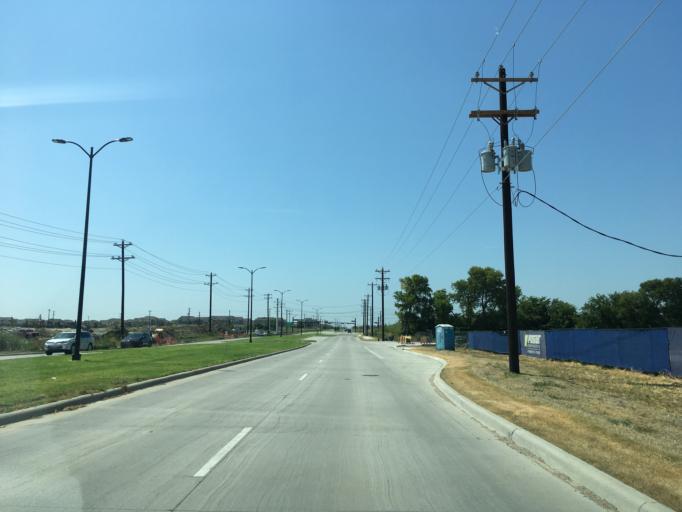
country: US
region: Texas
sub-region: Collin County
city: Prosper
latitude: 33.2070
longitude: -96.7678
